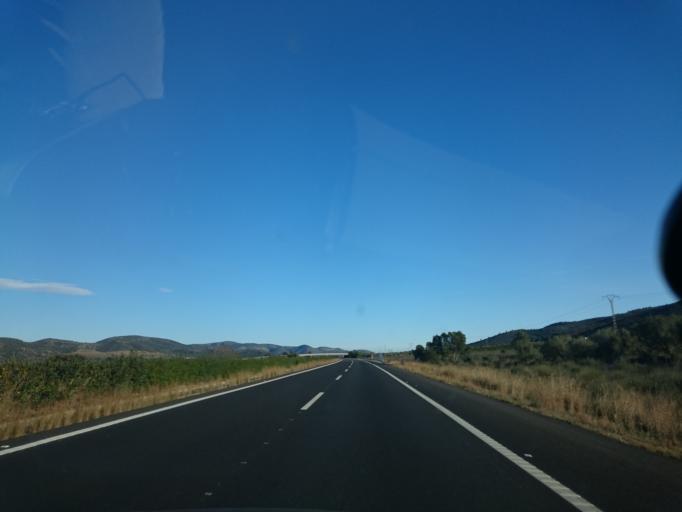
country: ES
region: Valencia
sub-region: Provincia de Castello
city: Alcala de Xivert
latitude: 40.3170
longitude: 0.2487
